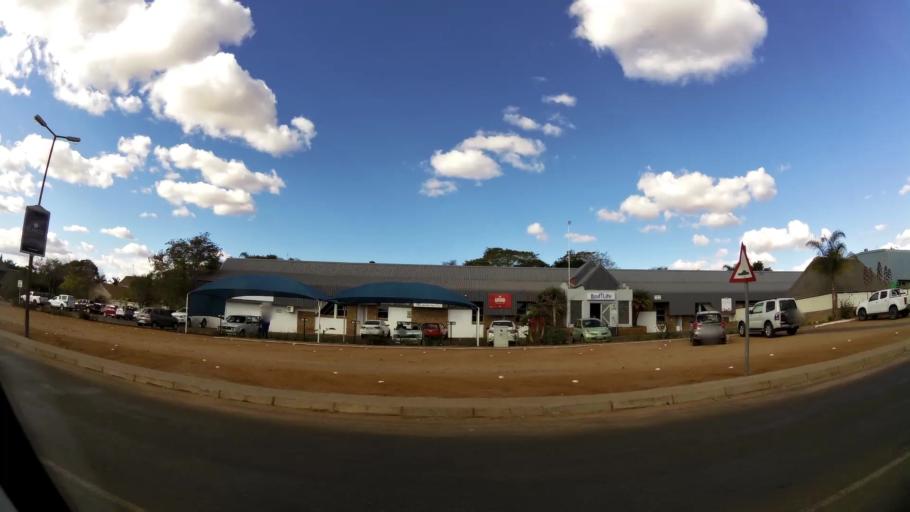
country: ZA
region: Limpopo
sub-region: Capricorn District Municipality
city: Polokwane
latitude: -23.8974
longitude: 29.4750
